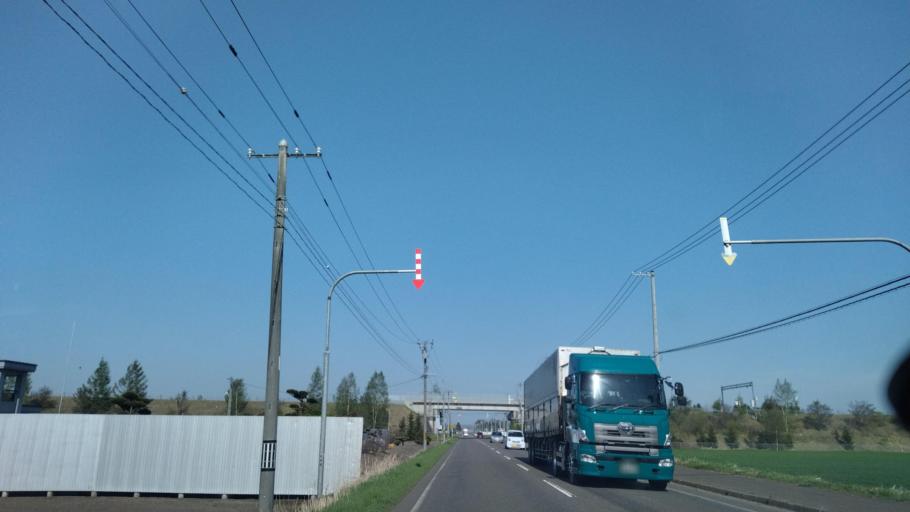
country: JP
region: Hokkaido
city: Obihiro
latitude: 42.9449
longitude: 143.1039
